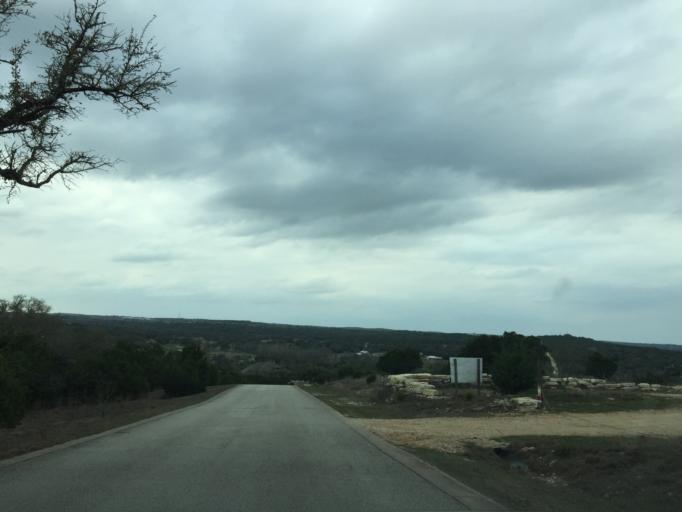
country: US
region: Texas
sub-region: Travis County
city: Shady Hollow
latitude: 30.1469
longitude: -97.9715
